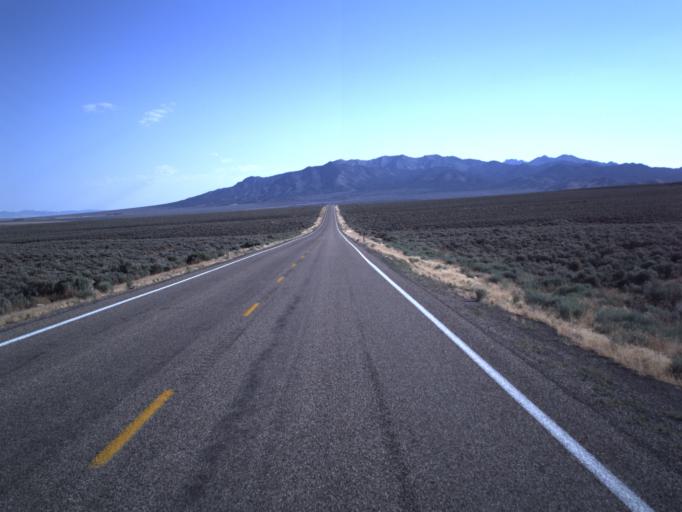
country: US
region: Utah
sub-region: Beaver County
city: Milford
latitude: 38.1532
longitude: -112.9588
